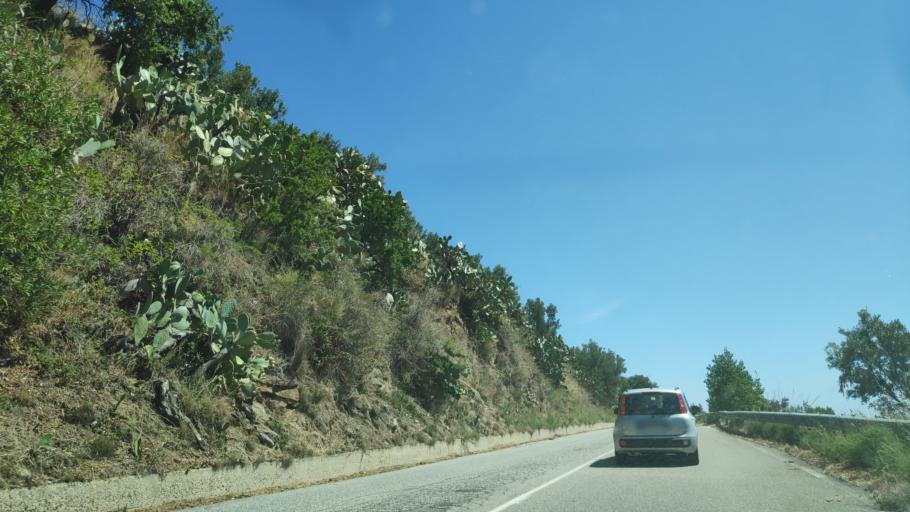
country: IT
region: Calabria
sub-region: Provincia di Catanzaro
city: Montauro
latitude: 38.7455
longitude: 16.5185
